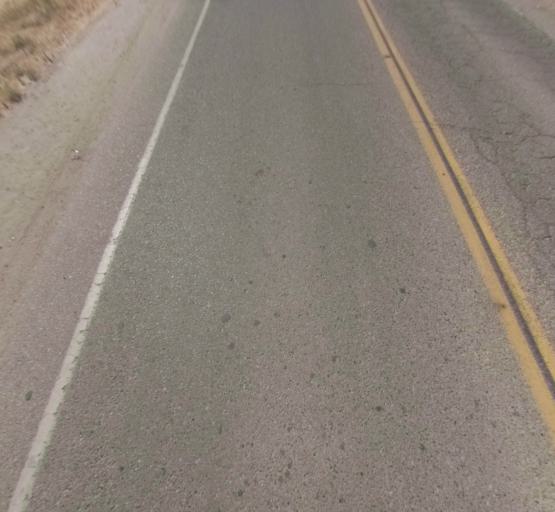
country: US
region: California
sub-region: Madera County
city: Chowchilla
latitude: 37.1267
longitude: -120.2591
